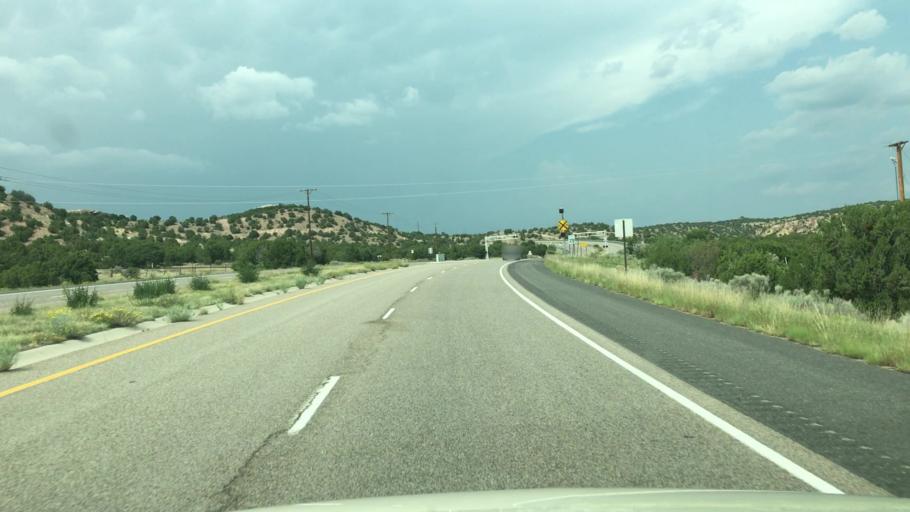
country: US
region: New Mexico
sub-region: Santa Fe County
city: Eldorado at Santa Fe
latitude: 35.4830
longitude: -105.9072
